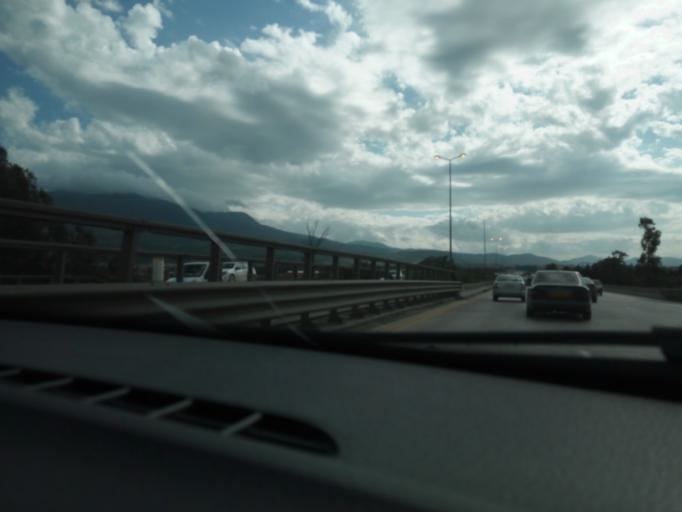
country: DZ
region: Blida
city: Chiffa
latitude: 36.4627
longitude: 2.7566
